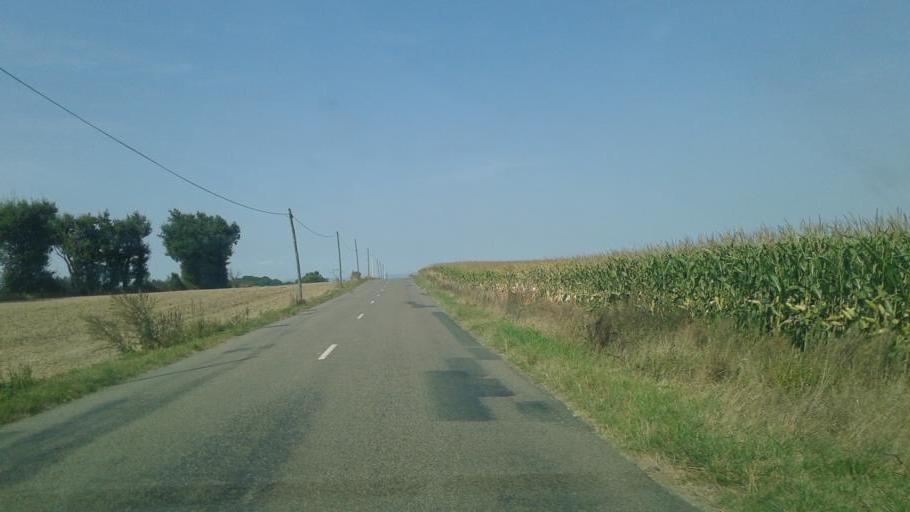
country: FR
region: Rhone-Alpes
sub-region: Departement de l'Ain
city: Tramoyes
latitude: 45.8724
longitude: 4.9872
